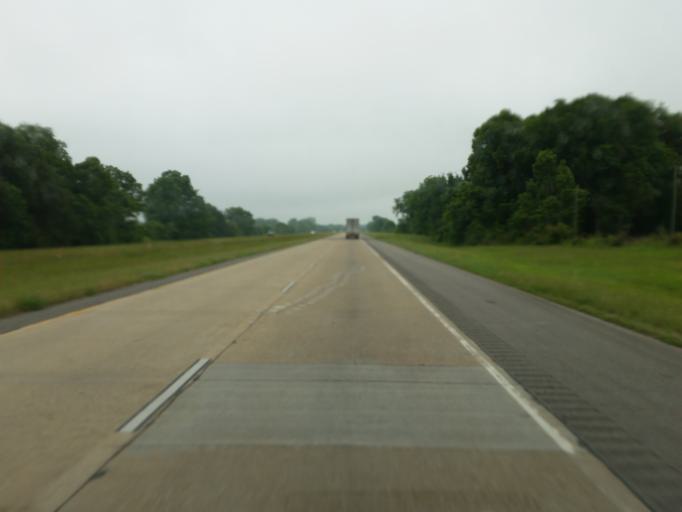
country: US
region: Louisiana
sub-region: Madison Parish
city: Tallulah
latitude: 32.3668
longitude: -91.1295
